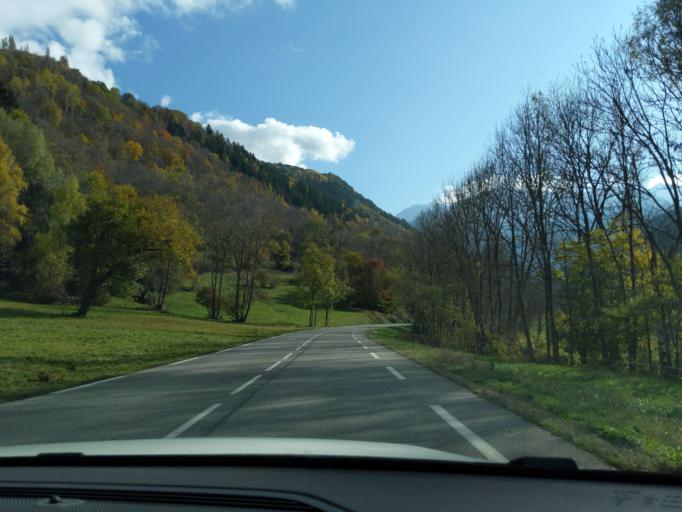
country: FR
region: Rhone-Alpes
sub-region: Departement de la Savoie
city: Seez
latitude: 45.6171
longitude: 6.8155
